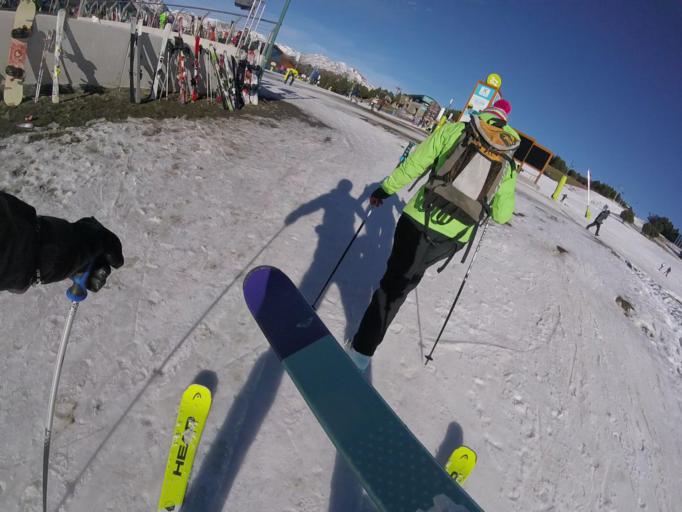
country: AD
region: Canillo
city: El Tarter
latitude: 42.5662
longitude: 1.6422
